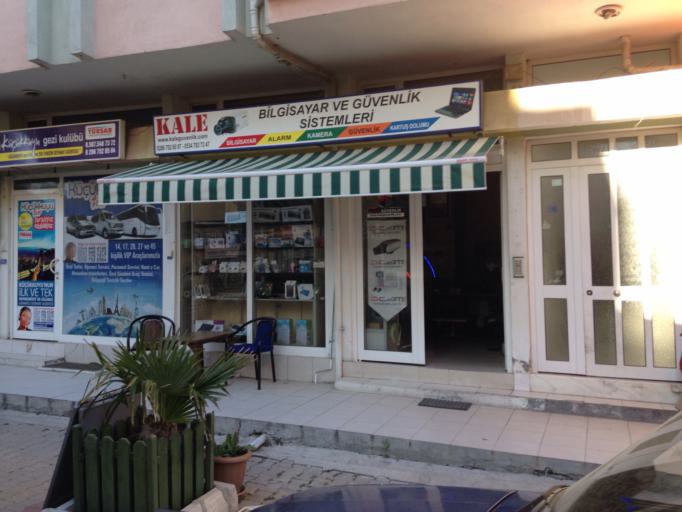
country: TR
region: Canakkale
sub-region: Merkez
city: Kucukkuyu
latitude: 39.5475
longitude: 26.6038
